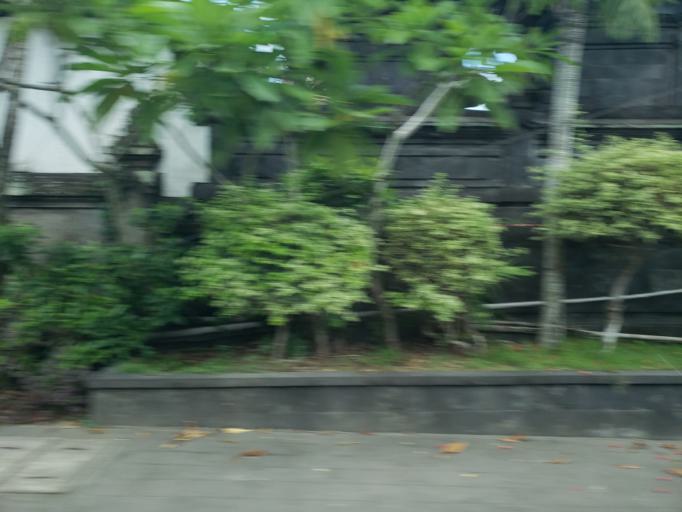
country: ID
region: Bali
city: Kangin
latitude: -8.8318
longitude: 115.1265
